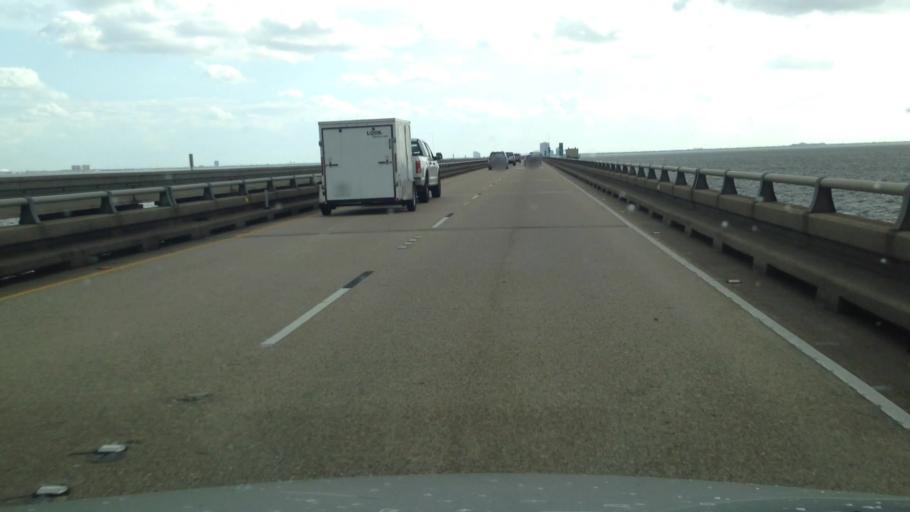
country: US
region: Louisiana
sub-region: Jefferson Parish
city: Metairie
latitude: 30.0931
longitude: -90.1417
